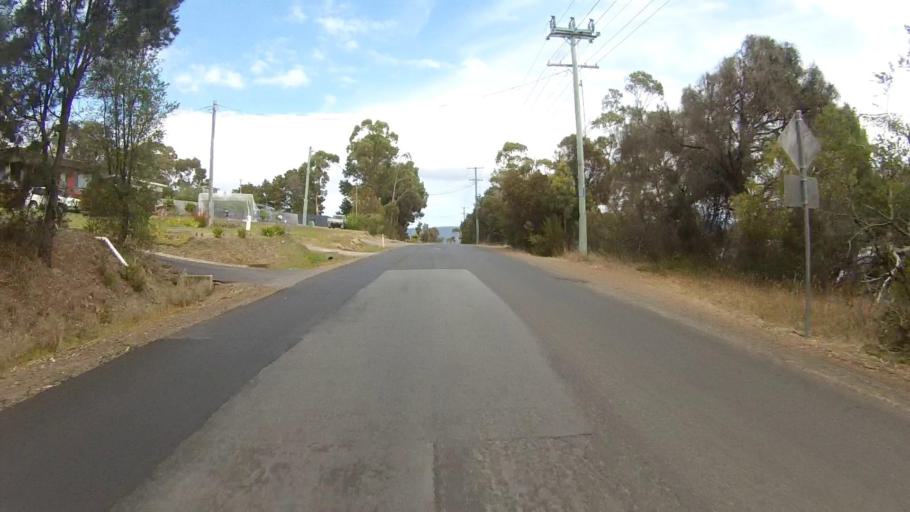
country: AU
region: Tasmania
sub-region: Kingborough
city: Margate
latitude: -43.0227
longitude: 147.2913
